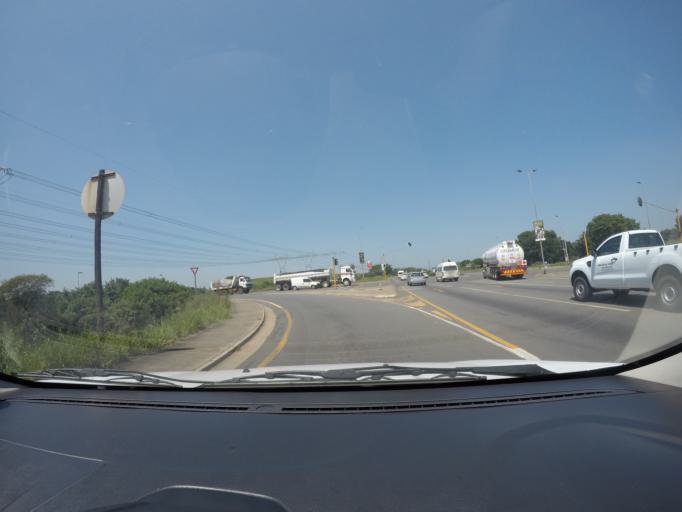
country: ZA
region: KwaZulu-Natal
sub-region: uThungulu District Municipality
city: Richards Bay
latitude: -28.7719
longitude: 32.0146
